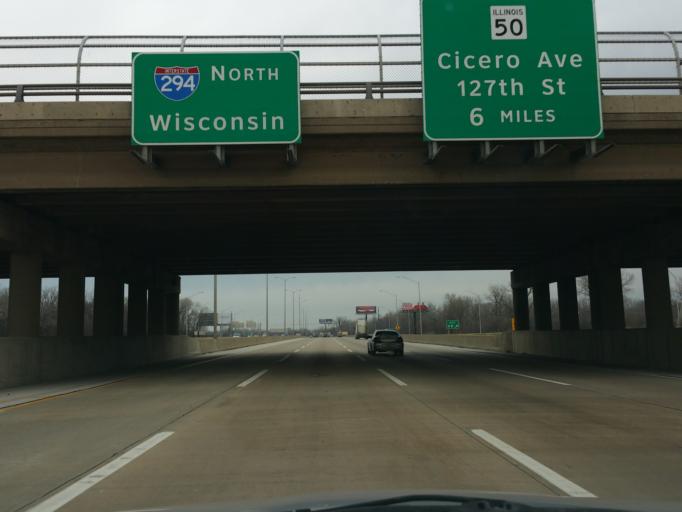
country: US
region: Illinois
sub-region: Cook County
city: University Park
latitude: 41.6009
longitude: -87.6810
